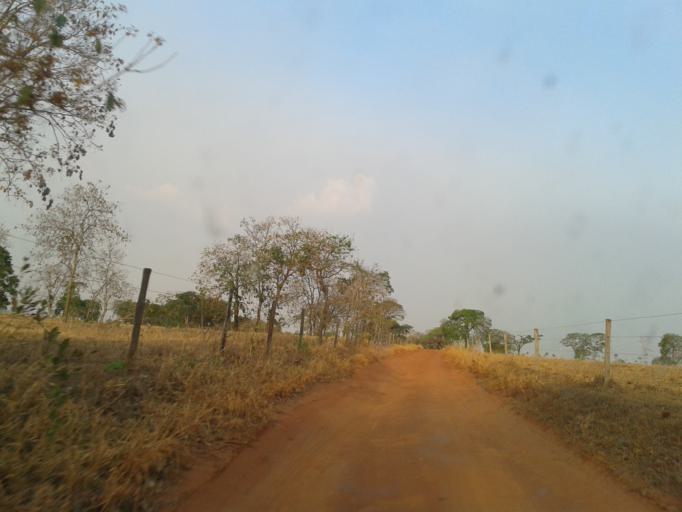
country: BR
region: Minas Gerais
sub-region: Capinopolis
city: Capinopolis
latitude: -18.8056
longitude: -49.7510
